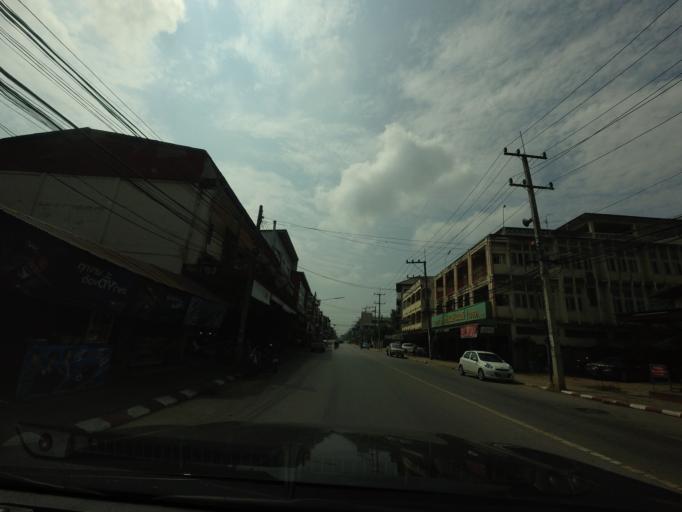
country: TH
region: Phrae
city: Phrae
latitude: 18.1497
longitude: 100.1493
